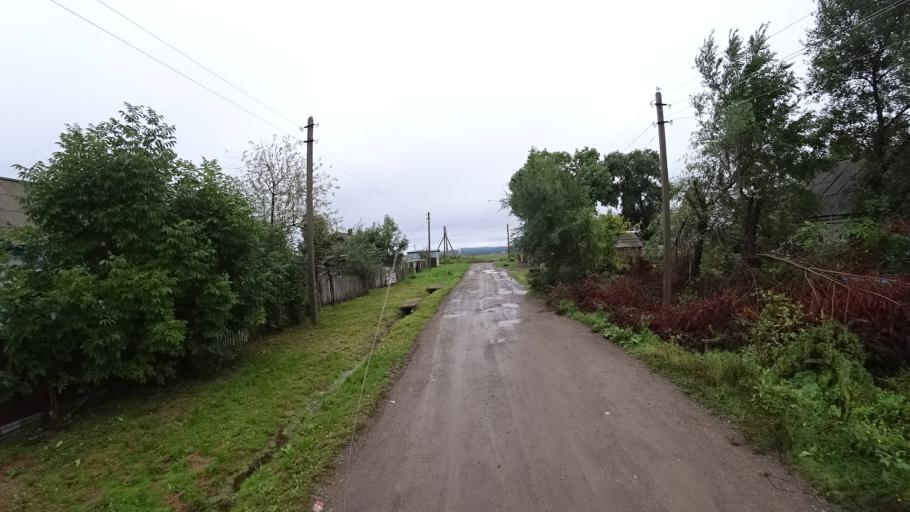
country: RU
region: Primorskiy
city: Monastyrishche
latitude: 44.2347
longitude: 132.4644
